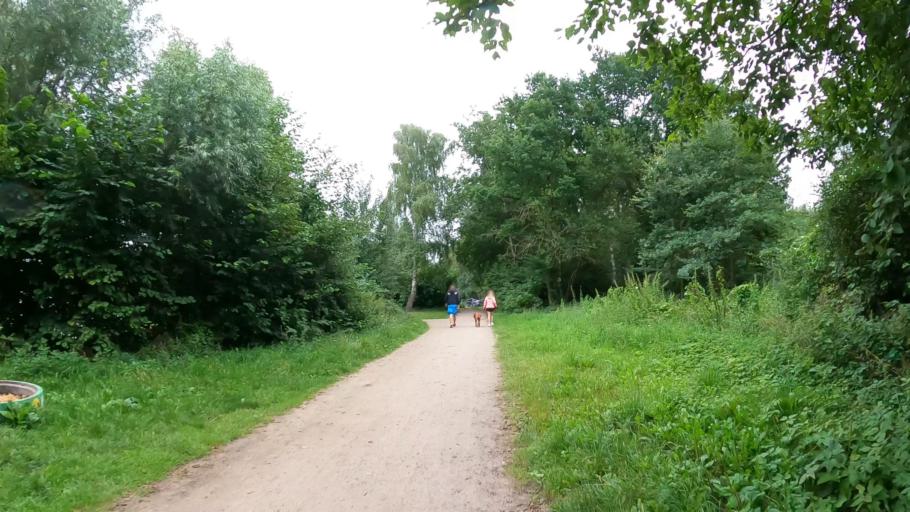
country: DE
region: Lower Saxony
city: Stelle
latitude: 53.4174
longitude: 10.0478
